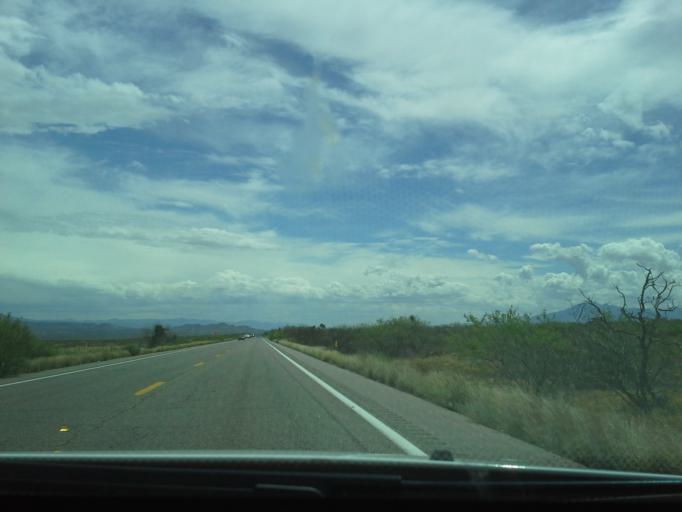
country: US
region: Arizona
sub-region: Gila County
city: Peridot
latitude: 33.3169
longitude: -110.5254
